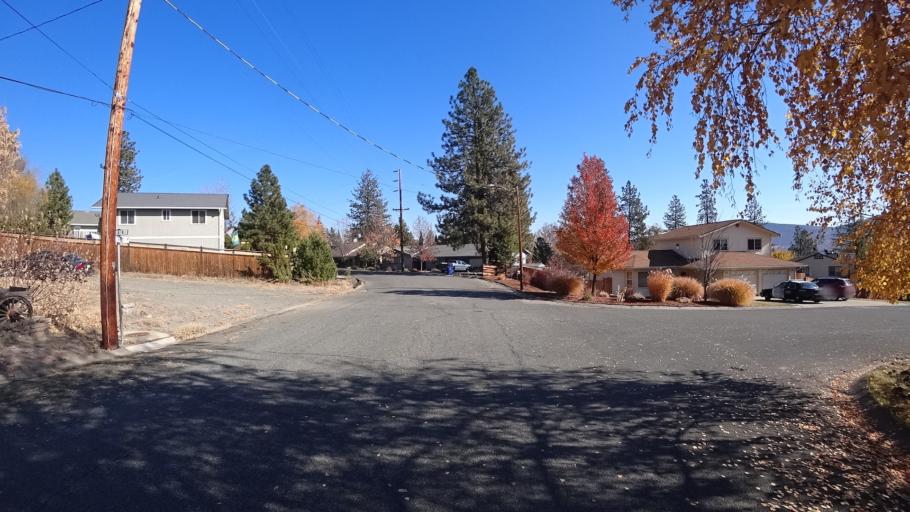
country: US
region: California
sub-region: Siskiyou County
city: Yreka
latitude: 41.7386
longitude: -122.6480
